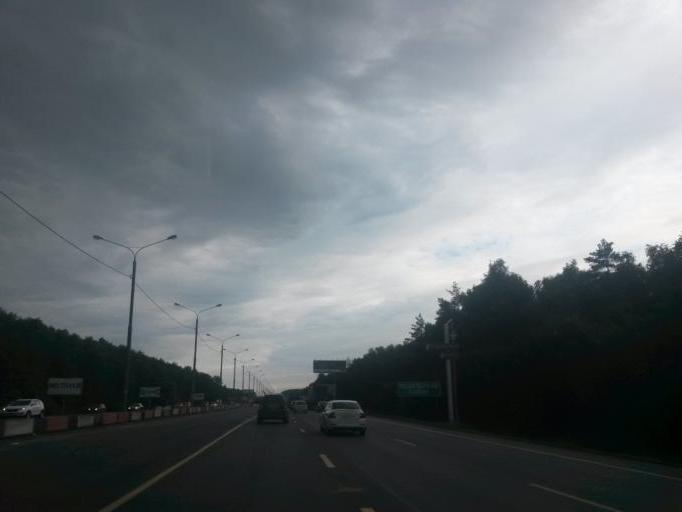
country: RU
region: Moskovskaya
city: Shcherbinka
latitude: 55.5104
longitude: 37.6087
